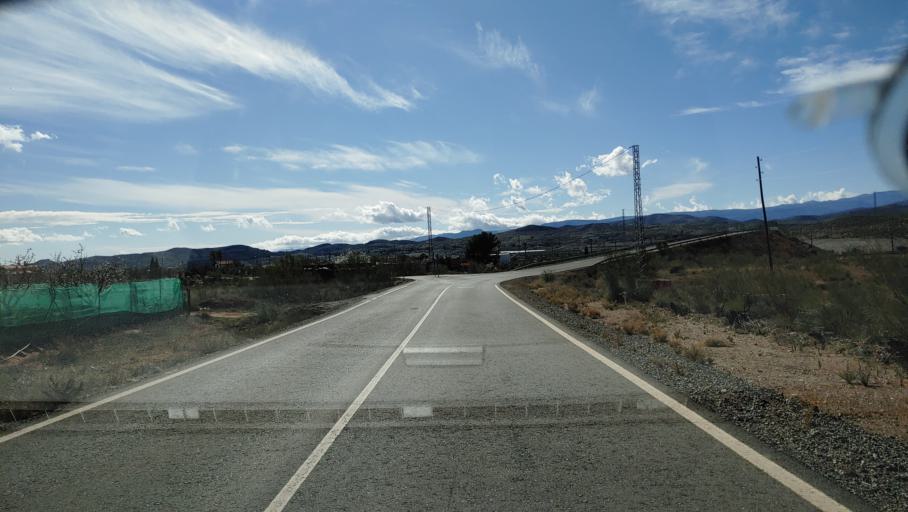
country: ES
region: Andalusia
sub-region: Provincia de Almeria
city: Gergal
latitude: 37.1125
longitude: -2.5924
